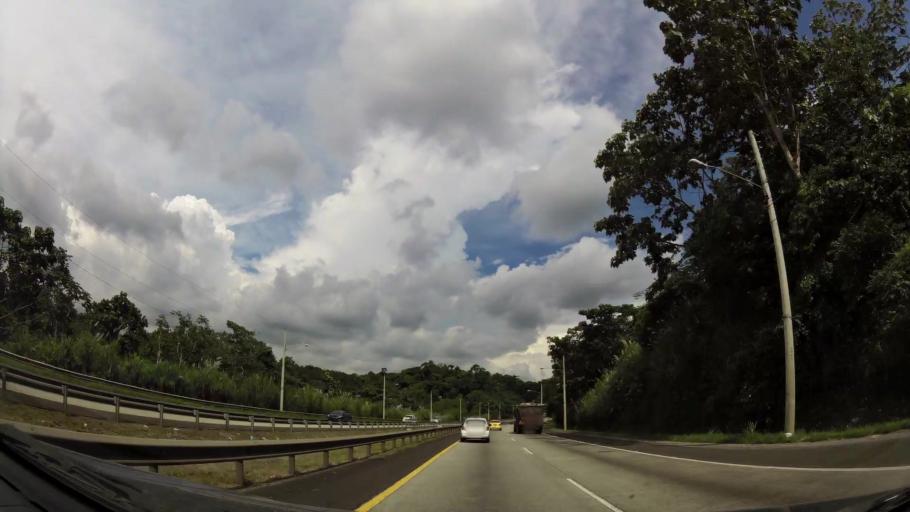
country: PA
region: Panama
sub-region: Distrito de Panama
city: Paraiso
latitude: 9.0398
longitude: -79.5708
